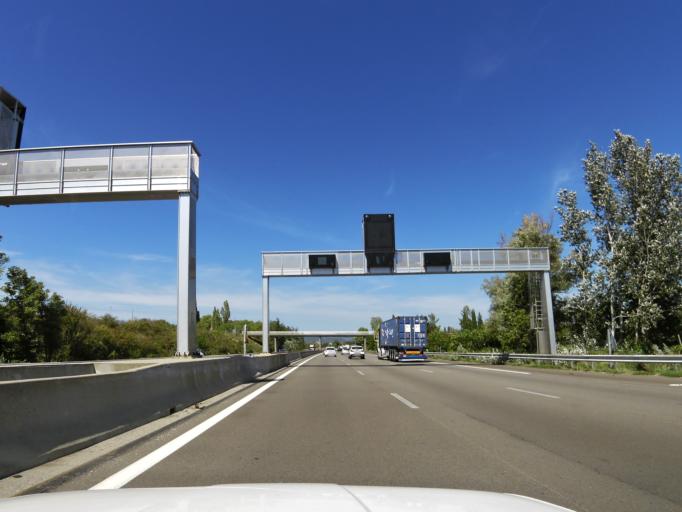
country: FR
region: Rhone-Alpes
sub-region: Departement de la Drome
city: Saulce-sur-Rhone
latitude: 44.7054
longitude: 4.7861
